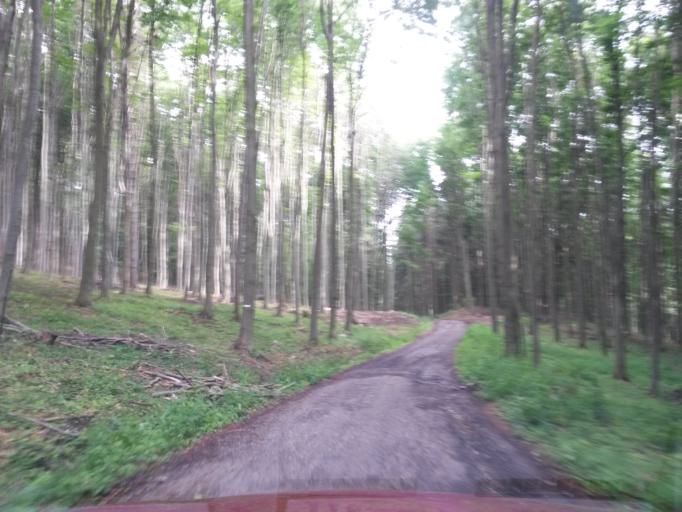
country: SK
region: Banskobystricky
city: Detva
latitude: 48.4619
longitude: 19.3027
